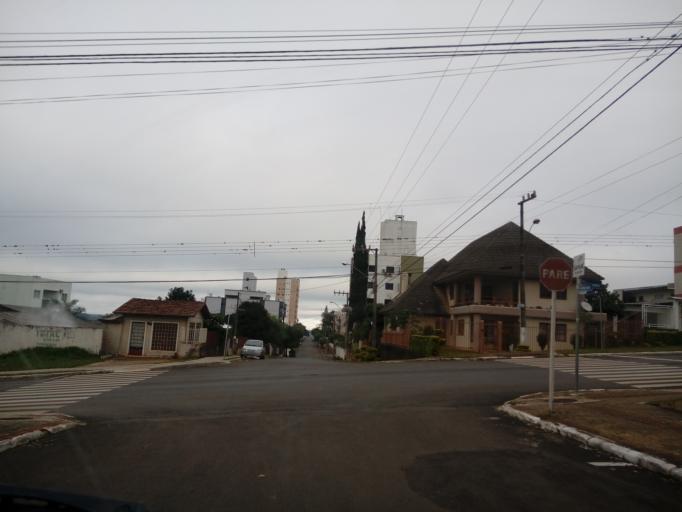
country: BR
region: Santa Catarina
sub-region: Chapeco
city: Chapeco
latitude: -27.0918
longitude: -52.6286
